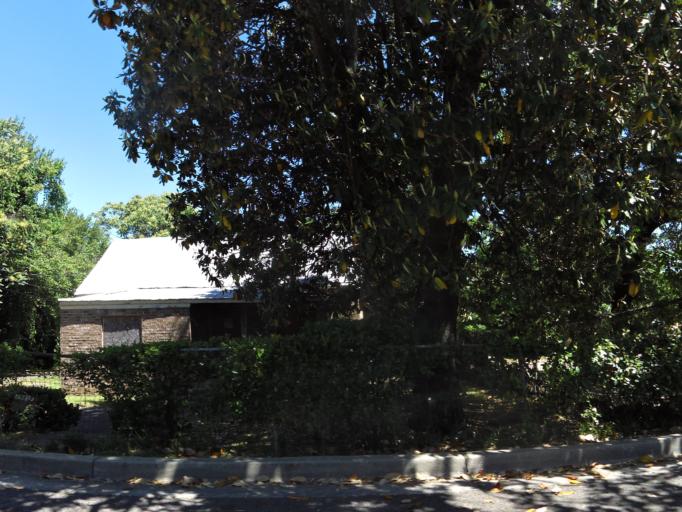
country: US
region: Georgia
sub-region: Richmond County
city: Augusta
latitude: 33.4826
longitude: -82.0228
